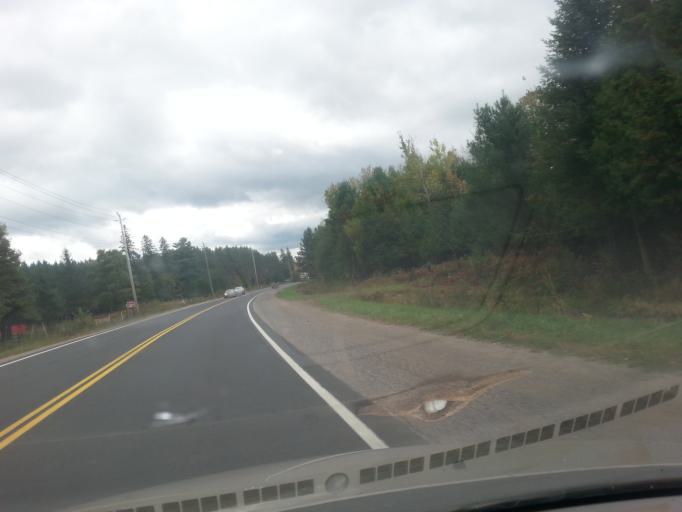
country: CA
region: Ontario
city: Pembroke
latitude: 45.5677
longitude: -77.1205
